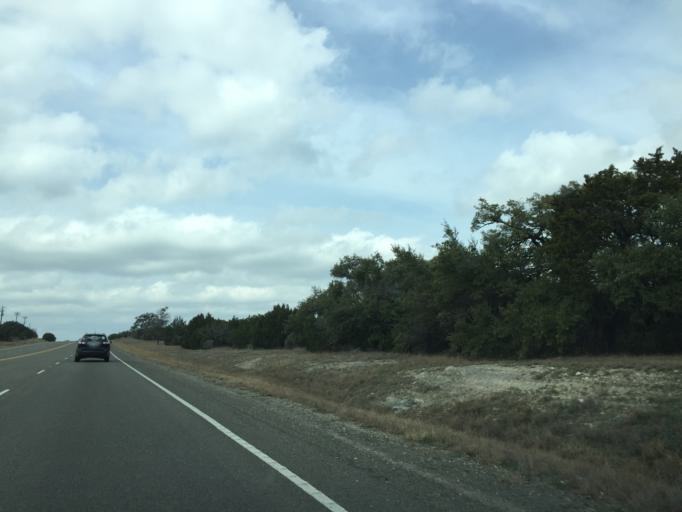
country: US
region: Texas
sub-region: Burnet County
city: Marble Falls
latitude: 30.4858
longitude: -98.2078
